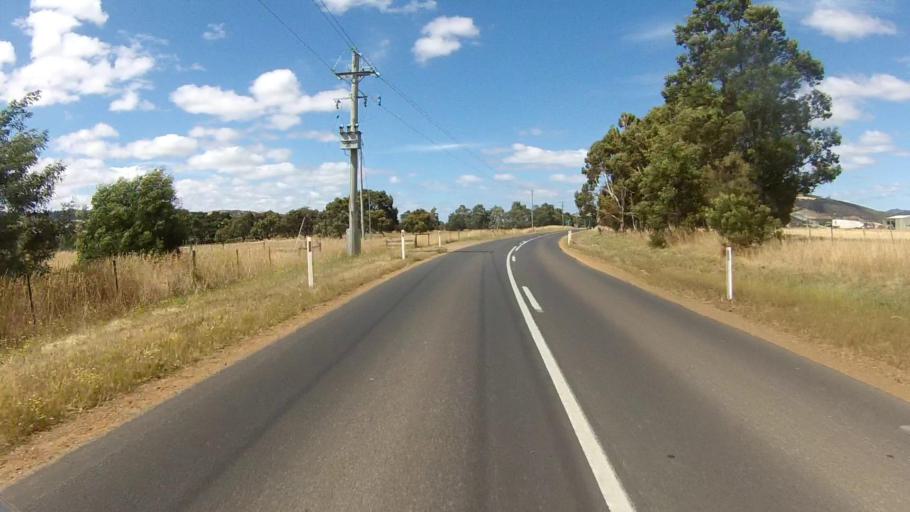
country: AU
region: Tasmania
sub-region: Clarence
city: Cambridge
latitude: -42.7239
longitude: 147.4355
